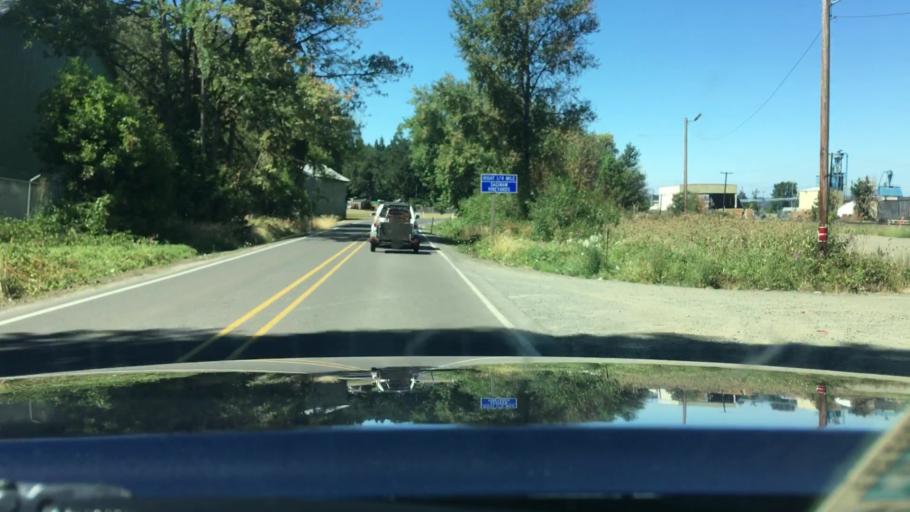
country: US
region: Oregon
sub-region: Lane County
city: Cottage Grove
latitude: 43.8291
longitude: -123.0448
